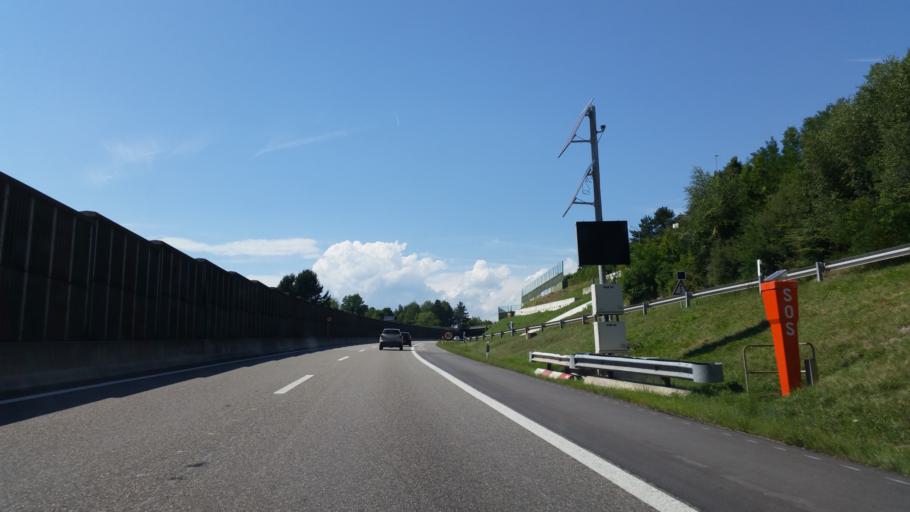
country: CH
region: Vaud
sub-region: Lavaux-Oron District
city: Belmont-sur-Lausanne
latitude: 46.5171
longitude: 6.6911
